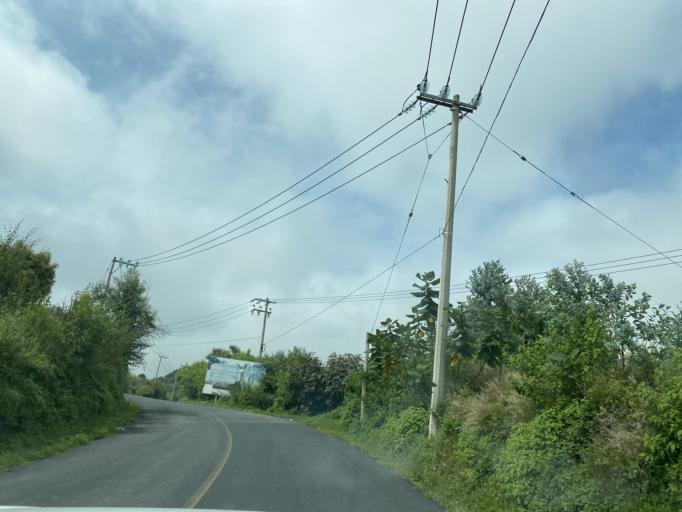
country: MX
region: Mexico
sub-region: Ozumba
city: San Jose Tlacotitlan
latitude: 18.9994
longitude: -98.8011
